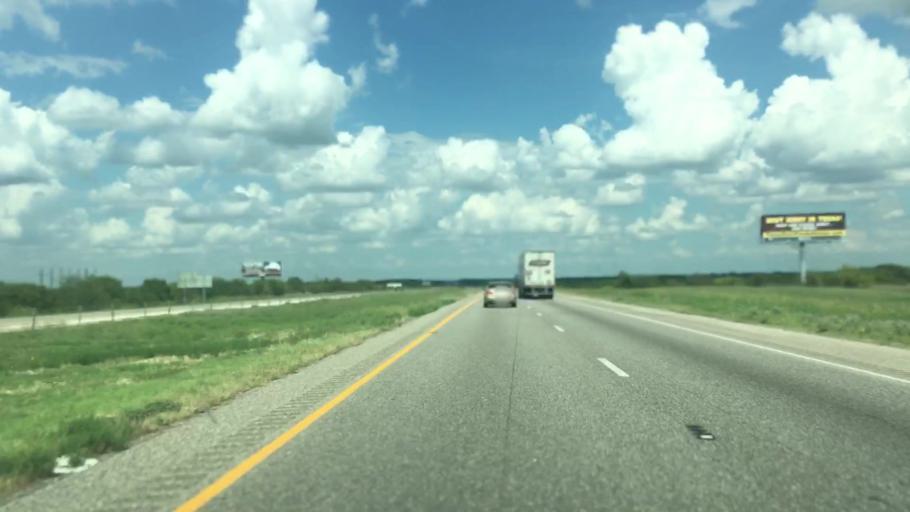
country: US
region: Texas
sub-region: Hill County
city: Hillsboro
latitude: 32.0819
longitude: -97.0466
